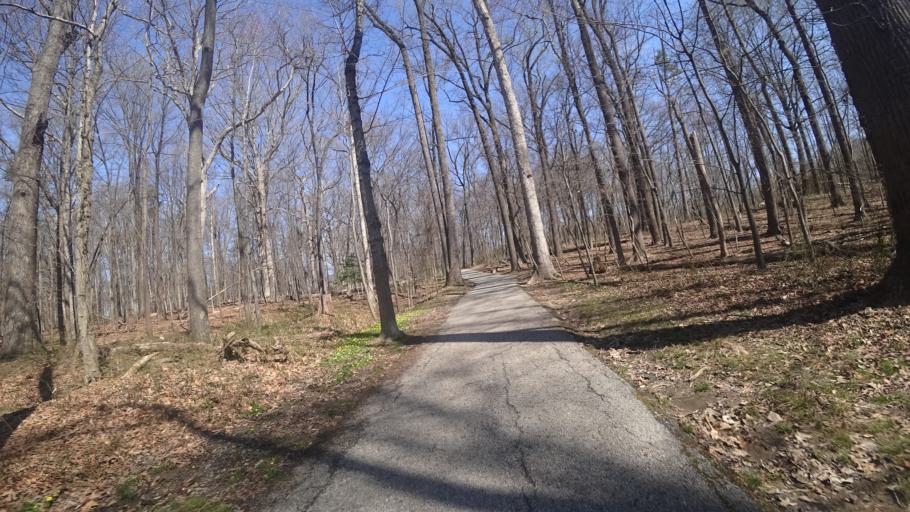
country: US
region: Maryland
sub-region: Montgomery County
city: Kemp Mill
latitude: 39.0424
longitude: -77.0360
